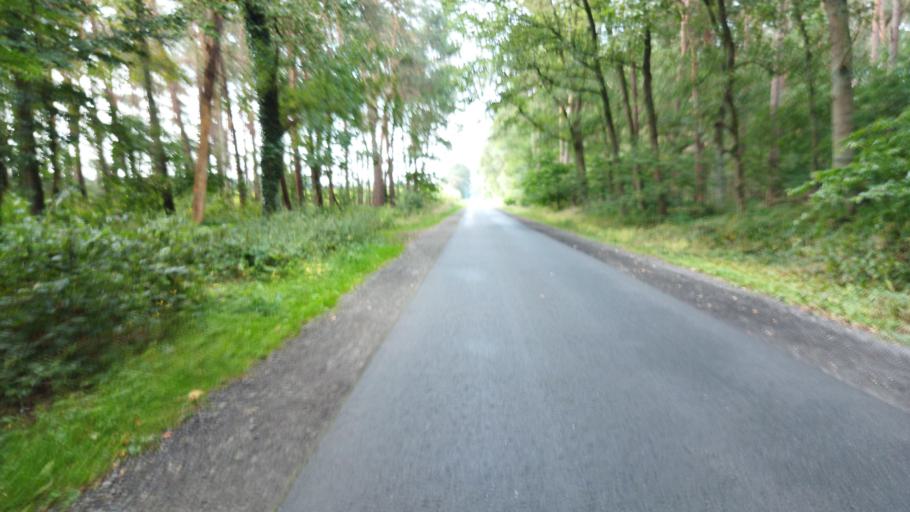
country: DE
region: North Rhine-Westphalia
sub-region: Regierungsbezirk Munster
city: Sassenberg
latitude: 52.0049
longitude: 8.0222
